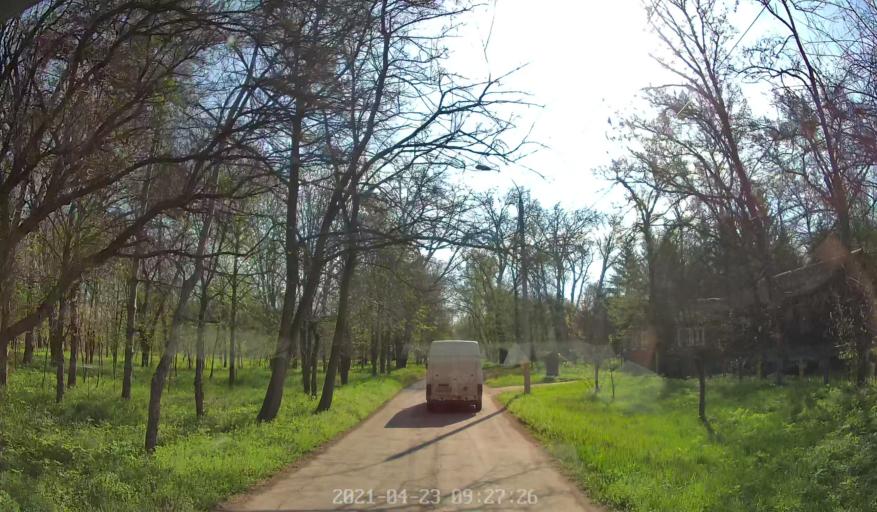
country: MD
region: Chisinau
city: Vadul lui Voda
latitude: 47.0864
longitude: 29.0999
